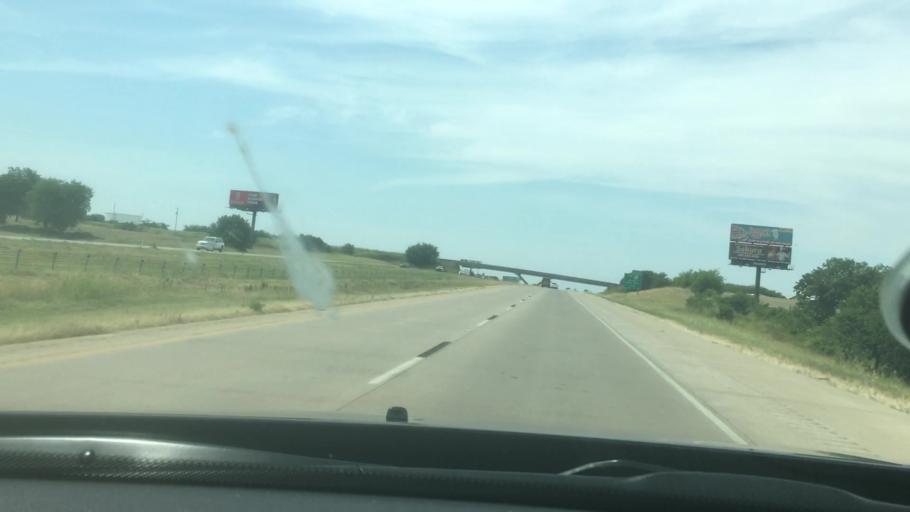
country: US
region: Oklahoma
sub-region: Carter County
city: Ardmore
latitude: 34.3220
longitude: -97.1559
